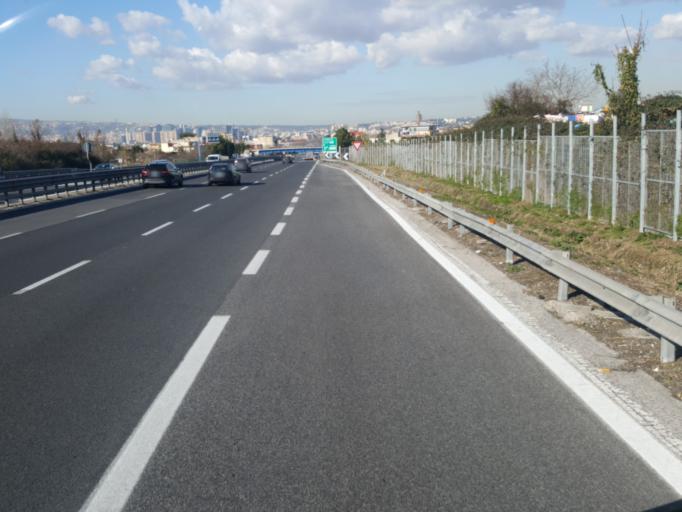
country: IT
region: Campania
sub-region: Provincia di Napoli
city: San Giorgio a Cremano
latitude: 40.8428
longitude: 14.3267
